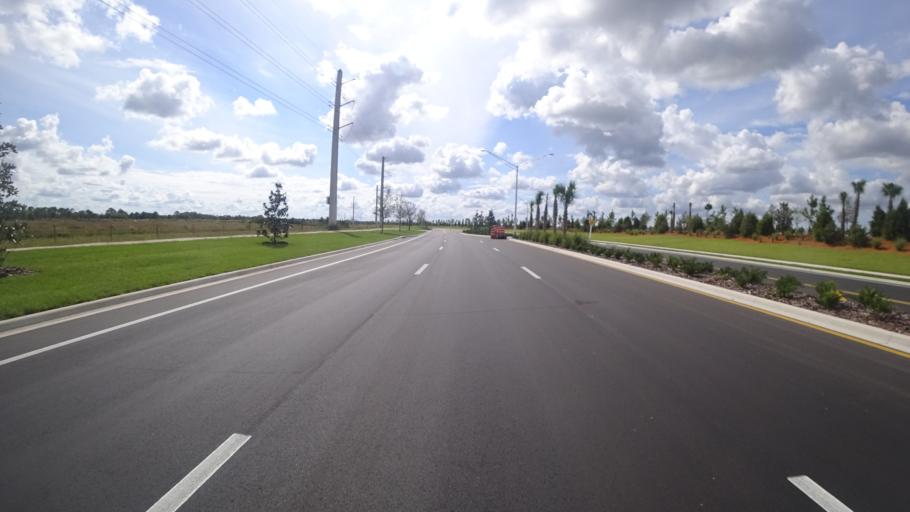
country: US
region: Florida
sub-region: Sarasota County
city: The Meadows
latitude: 27.4144
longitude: -82.3543
